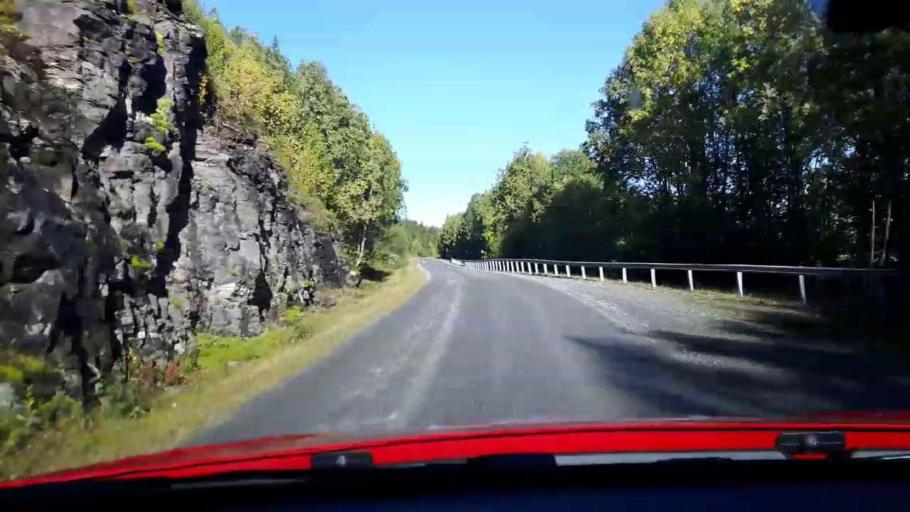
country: NO
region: Nord-Trondelag
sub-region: Lierne
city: Sandvika
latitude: 64.5727
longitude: 13.9017
